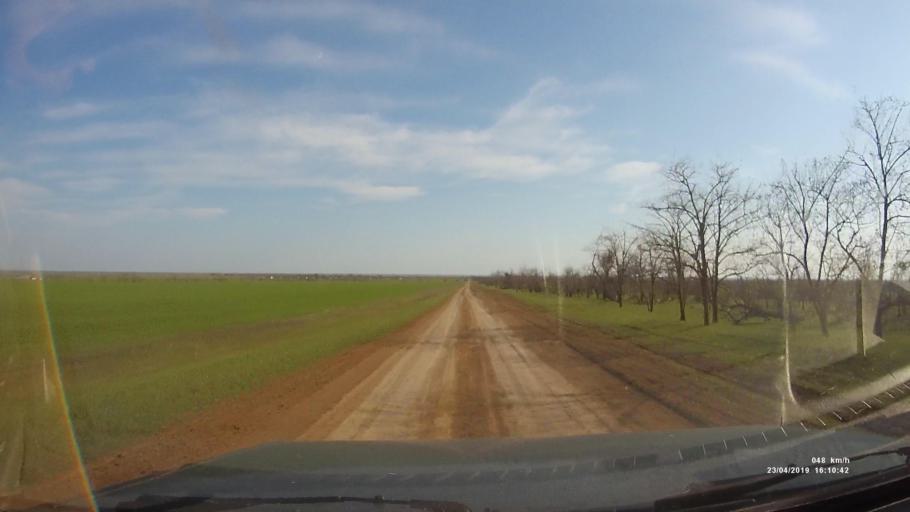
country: RU
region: Rostov
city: Remontnoye
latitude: 46.4802
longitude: 43.1231
